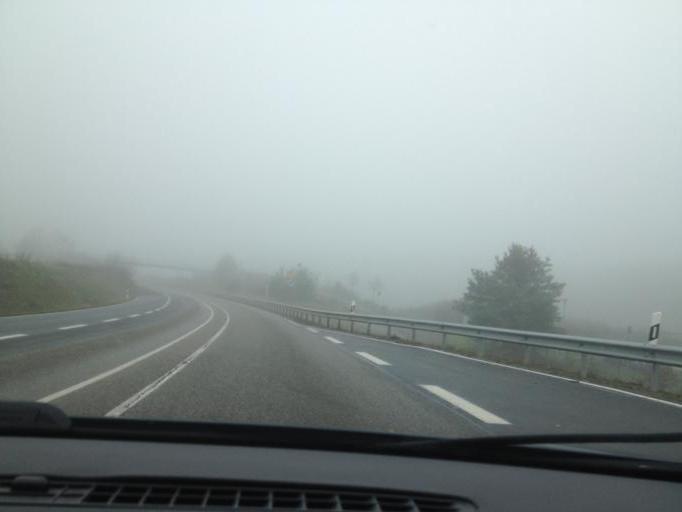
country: DE
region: Rheinland-Pfalz
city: Mackenbach
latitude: 49.4685
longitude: 7.5943
